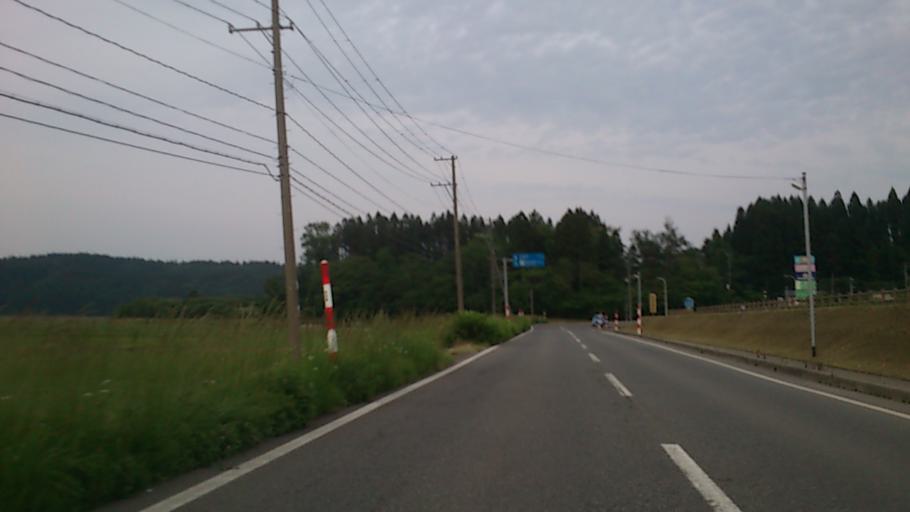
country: JP
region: Akita
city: Noshiromachi
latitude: 40.0905
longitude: 140.0850
